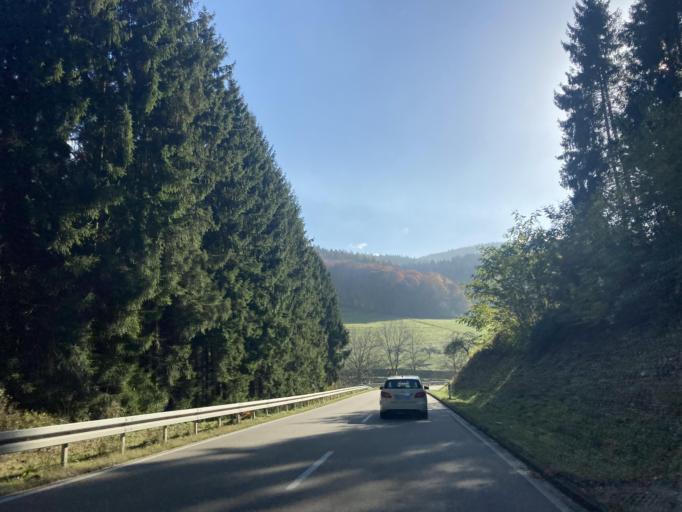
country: DE
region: Baden-Wuerttemberg
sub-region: Freiburg Region
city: Muhlenbach
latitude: 48.2179
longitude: 8.0950
